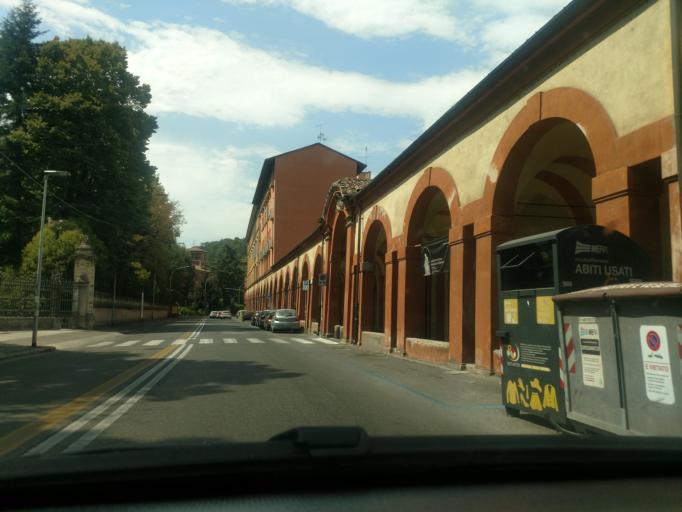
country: IT
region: Emilia-Romagna
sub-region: Provincia di Bologna
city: Bologna
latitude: 44.4893
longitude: 11.3194
